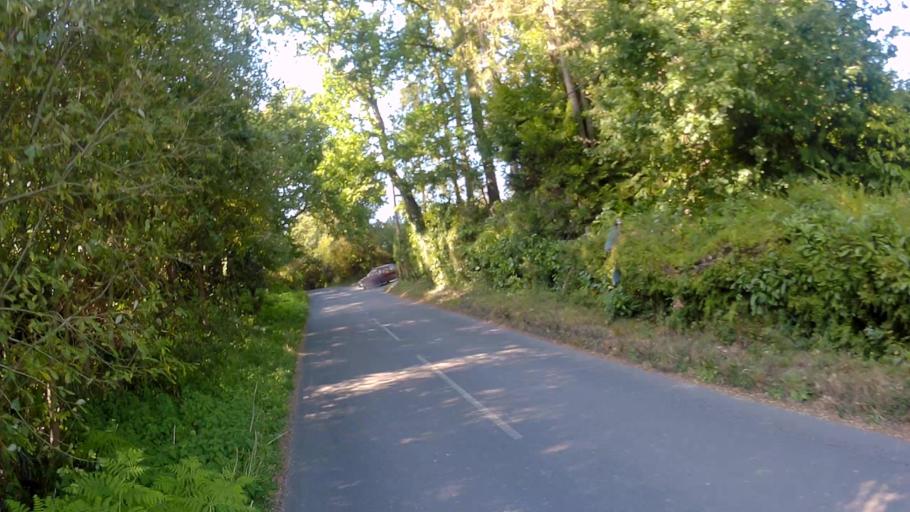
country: GB
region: England
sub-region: Hampshire
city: Lindford
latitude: 51.1598
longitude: -0.8325
